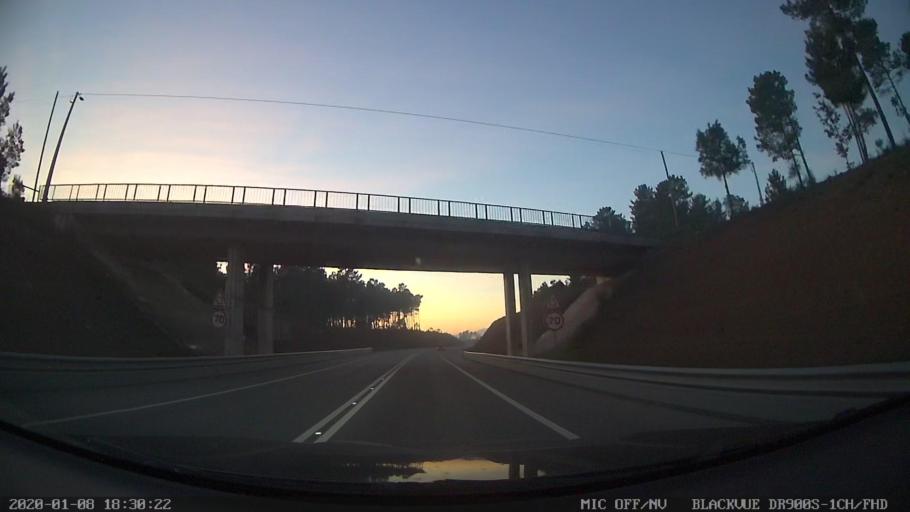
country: PT
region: Vila Real
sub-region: Vila Real
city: Vila Real
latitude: 41.2713
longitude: -7.6895
